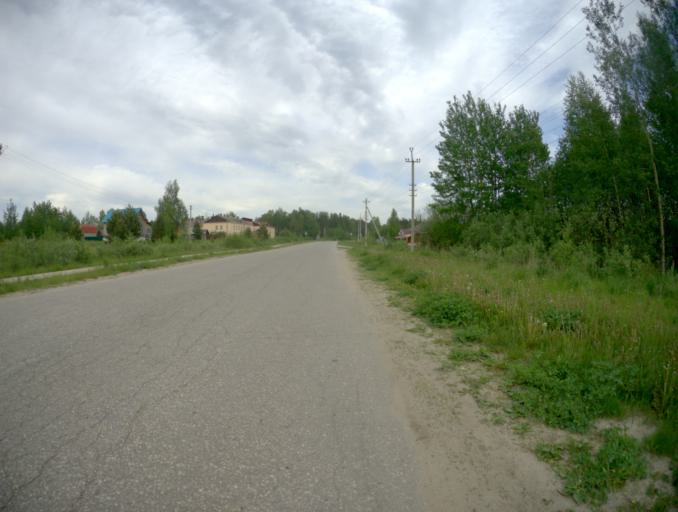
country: RU
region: Vladimir
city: Ivanishchi
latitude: 55.7779
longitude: 40.4285
